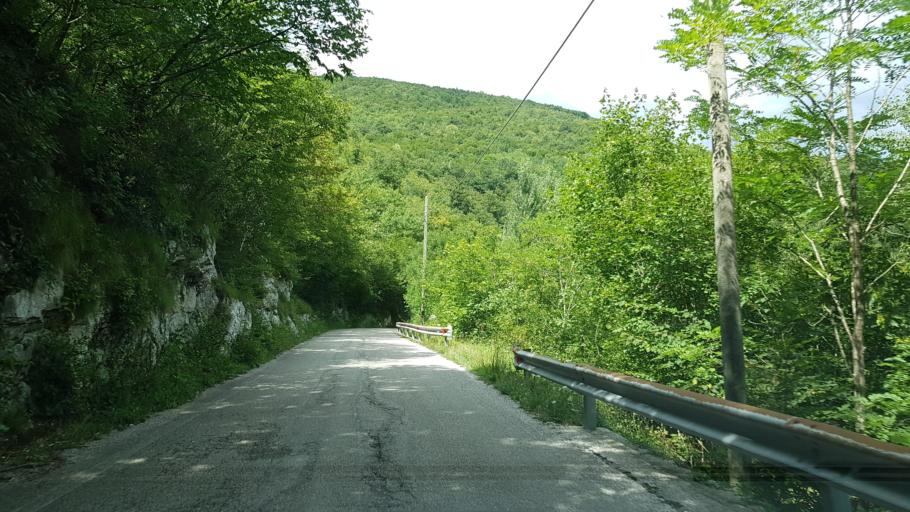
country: IT
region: Friuli Venezia Giulia
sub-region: Provincia di Udine
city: San Leonardo
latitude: 46.0686
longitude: 13.5292
